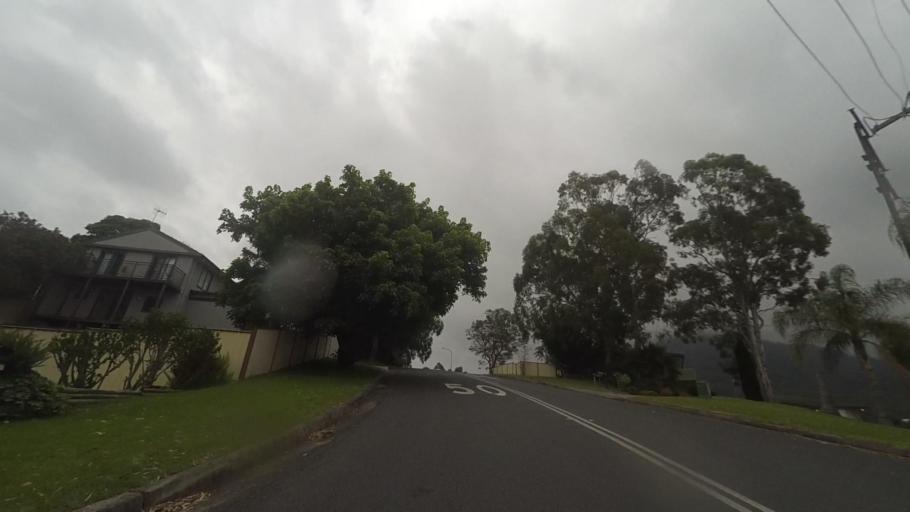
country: AU
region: New South Wales
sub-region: Wollongong
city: Cordeaux Heights
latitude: -34.4540
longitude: 150.8200
